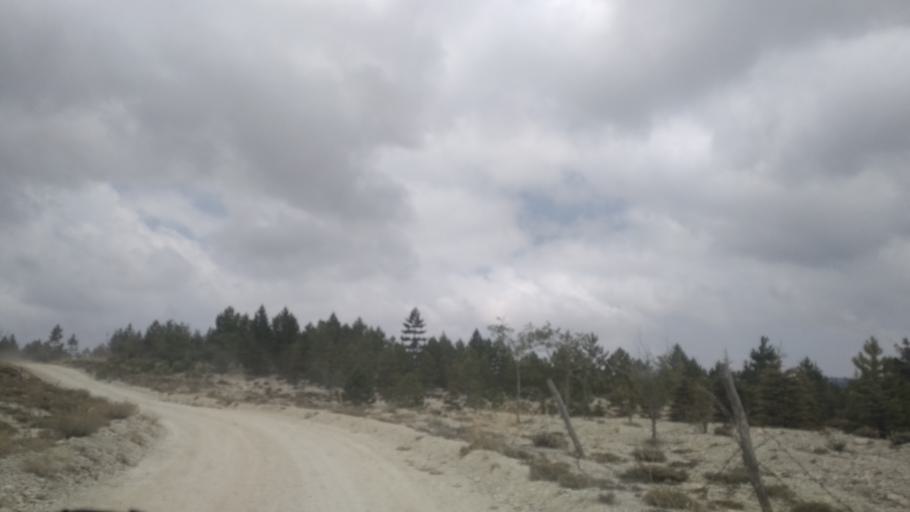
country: TR
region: Mersin
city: Sarikavak
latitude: 36.5741
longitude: 33.7600
